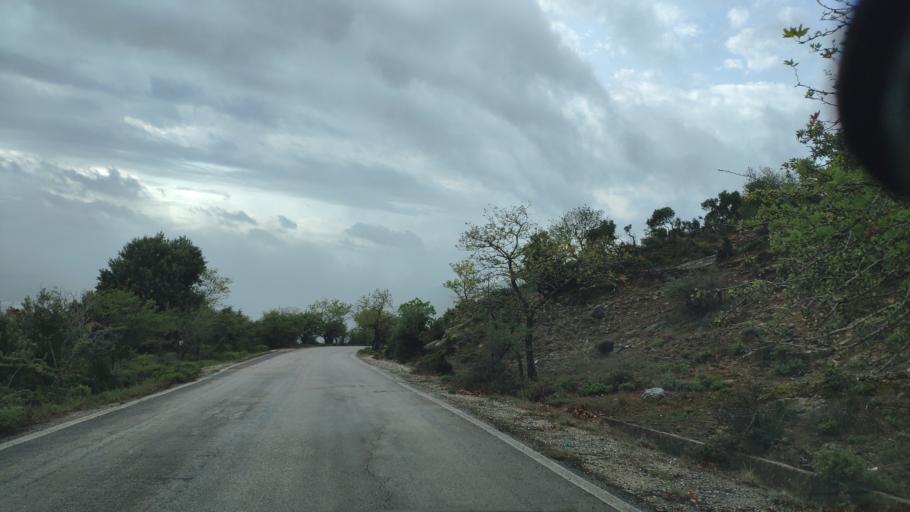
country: GR
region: West Greece
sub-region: Nomos Aitolias kai Akarnanias
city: Sardinia
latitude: 38.8516
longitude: 21.3148
